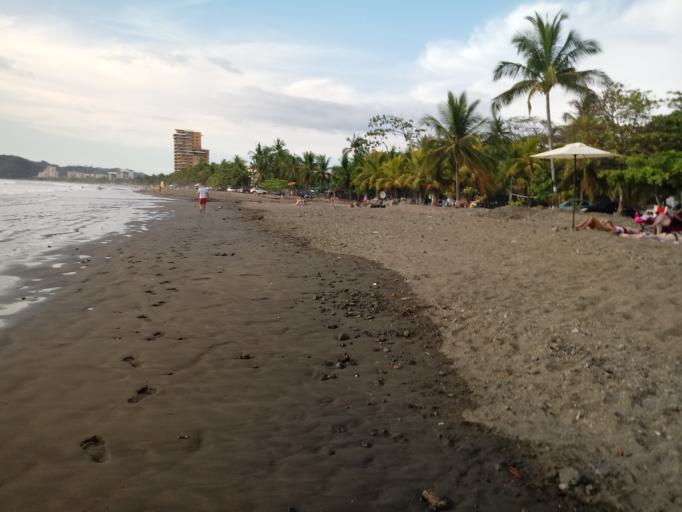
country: CR
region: Puntarenas
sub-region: Canton de Garabito
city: Jaco
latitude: 9.6054
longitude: -84.6235
